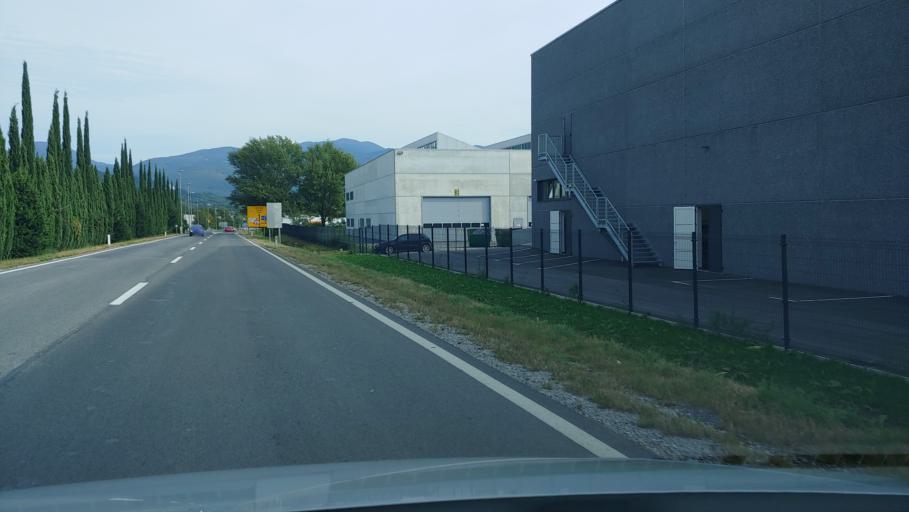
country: SI
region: Ajdovscina
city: Ajdovscina
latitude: 45.8822
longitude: 13.8984
